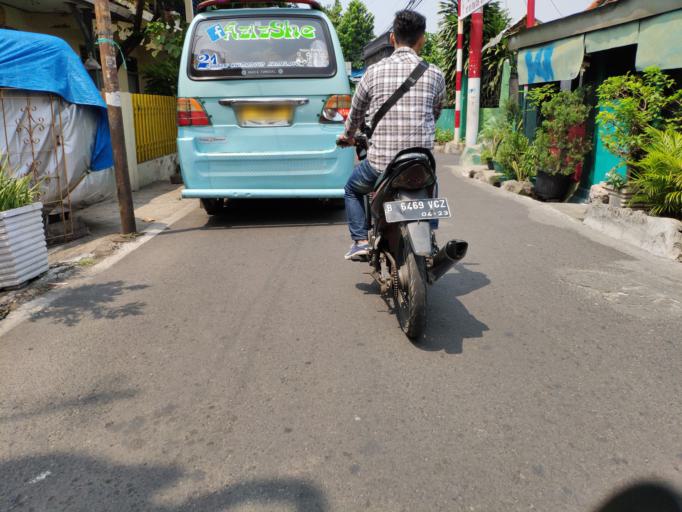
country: ID
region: Jakarta Raya
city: Jakarta
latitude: -6.2050
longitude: 106.8673
